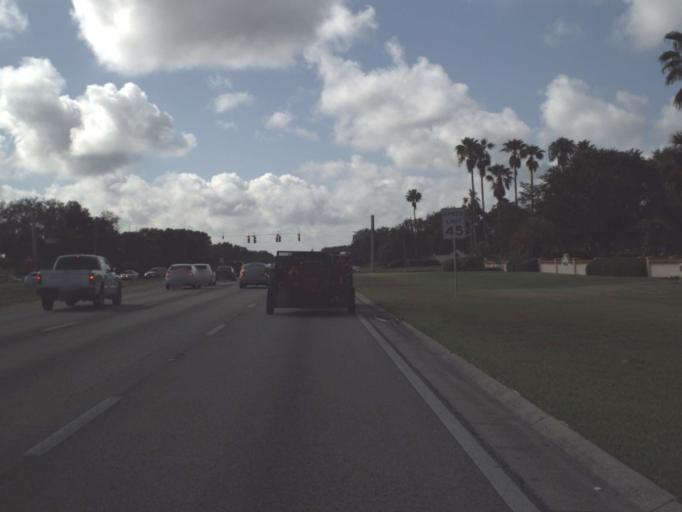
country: US
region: Florida
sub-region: Sumter County
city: The Villages
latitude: 28.9501
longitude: -81.9554
